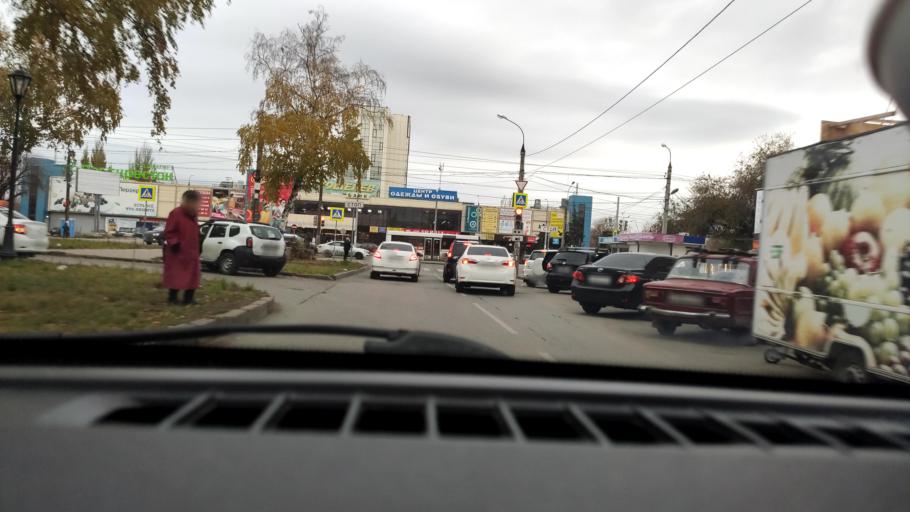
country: RU
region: Samara
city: Samara
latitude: 53.1920
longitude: 50.1789
